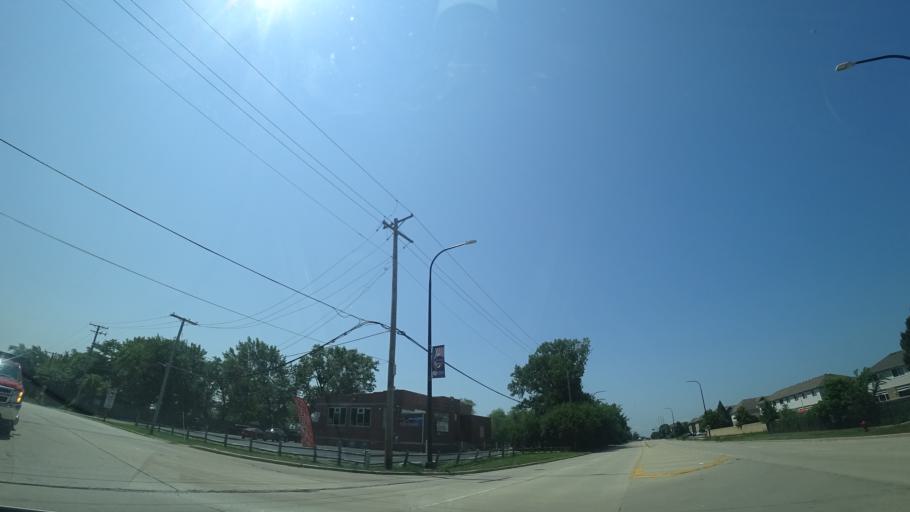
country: US
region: Illinois
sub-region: Cook County
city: Alsip
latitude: 41.6834
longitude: -87.7491
